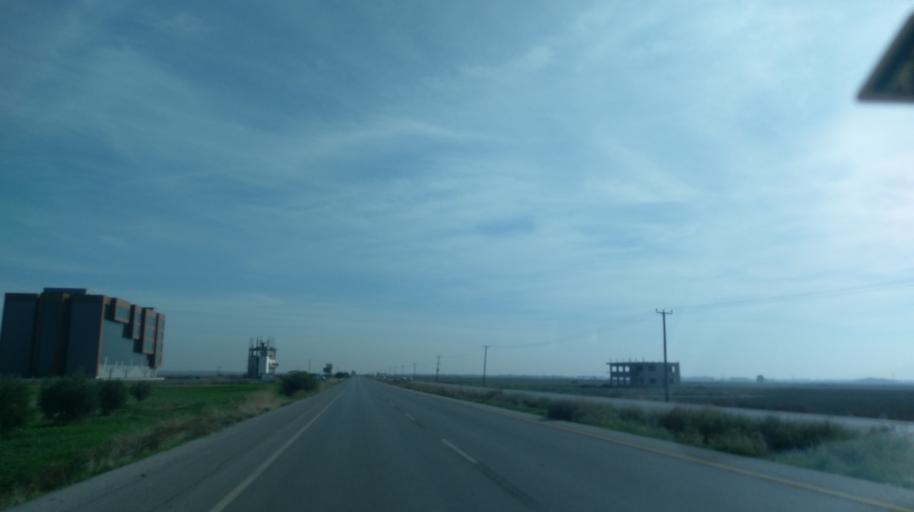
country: CY
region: Larnaka
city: Athienou
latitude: 35.2120
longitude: 33.5312
